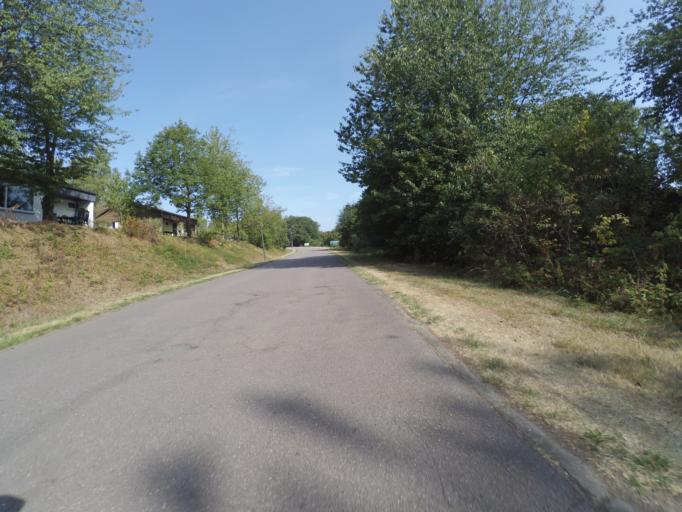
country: DE
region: Rheinland-Pfalz
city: Saarburg
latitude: 49.6172
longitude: 6.5444
